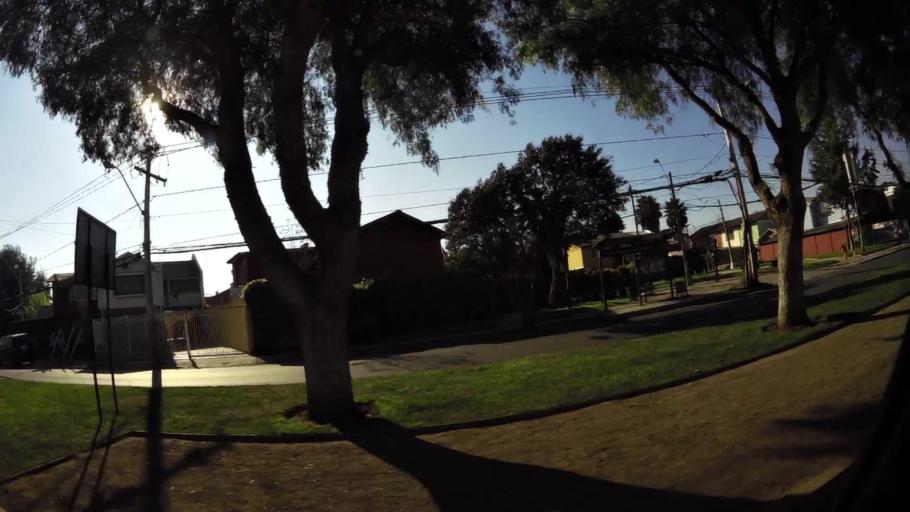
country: CL
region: Santiago Metropolitan
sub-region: Provincia de Santiago
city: Lo Prado
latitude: -33.4906
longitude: -70.7690
